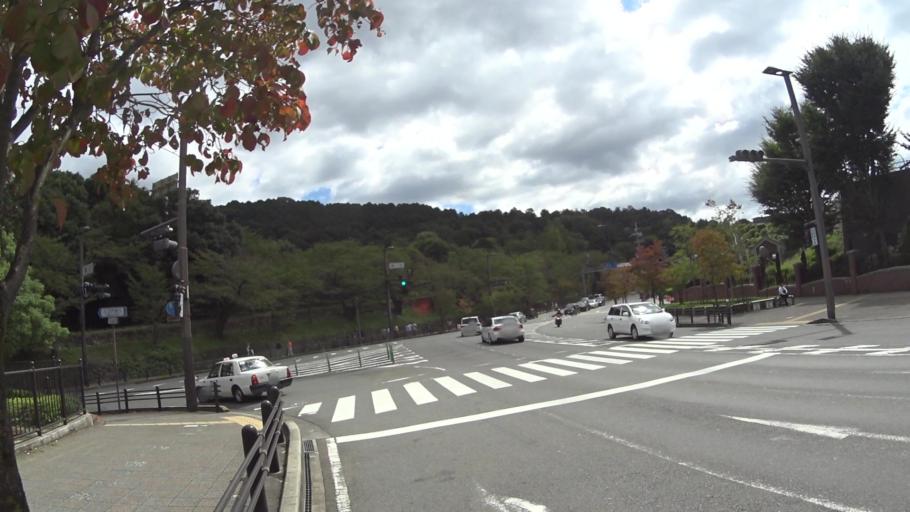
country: JP
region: Kyoto
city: Kyoto
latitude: 35.0093
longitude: 135.7893
